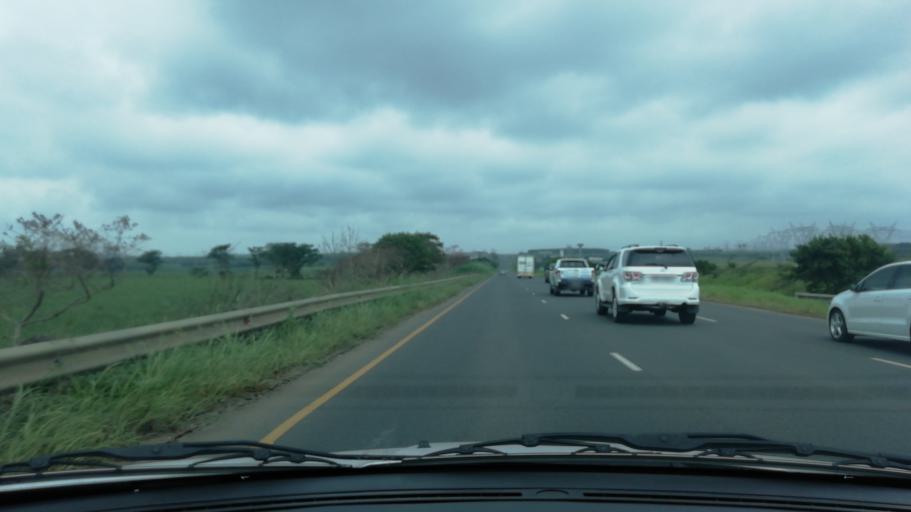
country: ZA
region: KwaZulu-Natal
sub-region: uThungulu District Municipality
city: Empangeni
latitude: -28.7733
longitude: 31.9489
